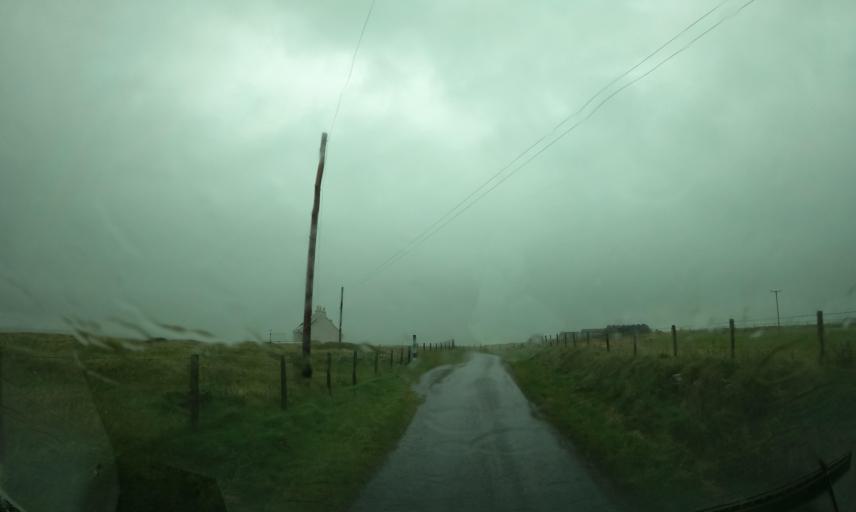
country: GB
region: Scotland
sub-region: Eilean Siar
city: Barra
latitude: 56.4559
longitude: -6.9403
